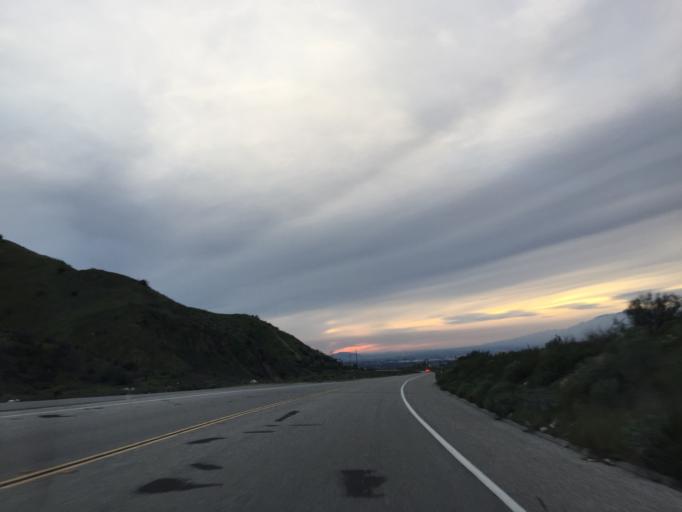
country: US
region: California
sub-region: San Bernardino County
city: Yucaipa
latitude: 34.0762
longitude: -117.0562
